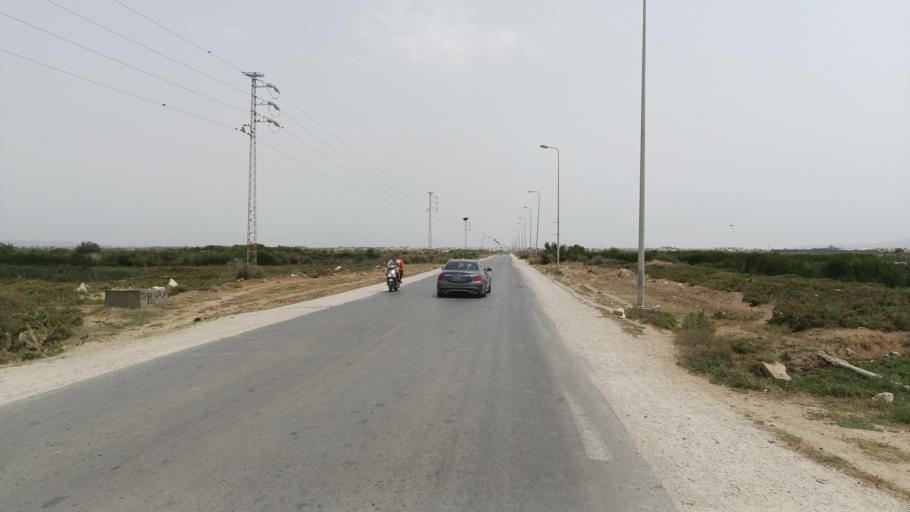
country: TN
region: Nabul
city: Manzil Bu Zalafah
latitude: 36.7241
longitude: 10.4716
